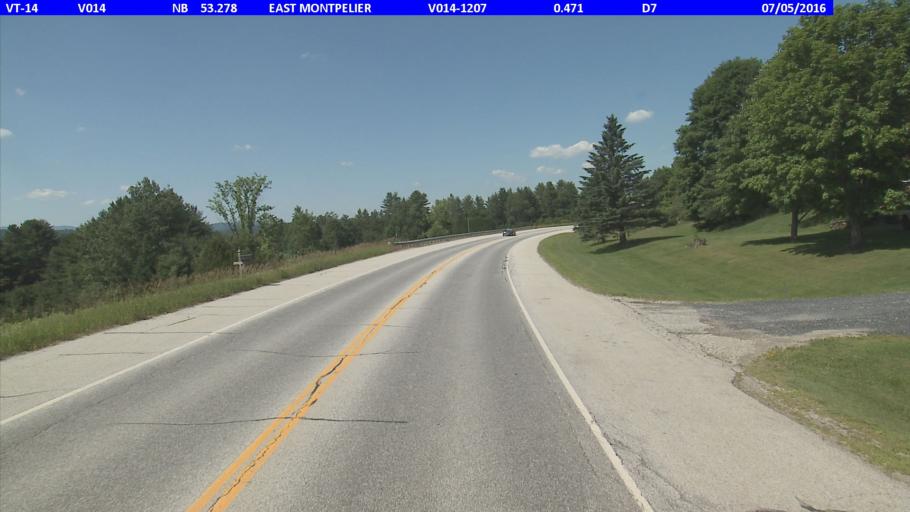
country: US
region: Vermont
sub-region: Washington County
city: Barre
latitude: 44.2421
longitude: -72.4897
